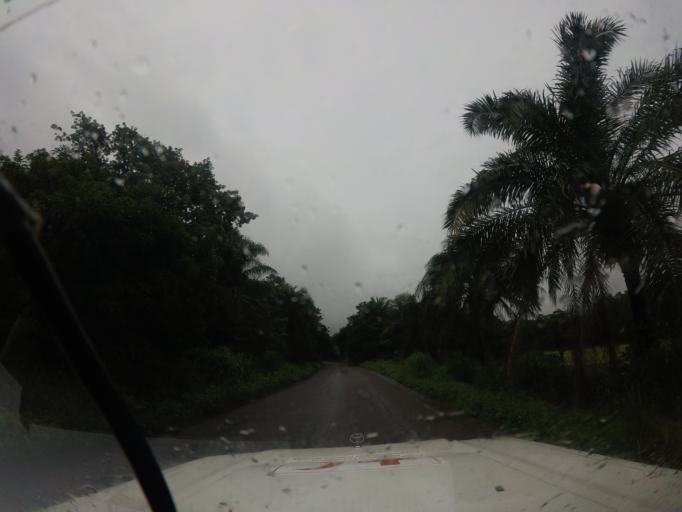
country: SL
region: Northern Province
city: Bumbuna
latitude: 9.3033
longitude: -11.9470
